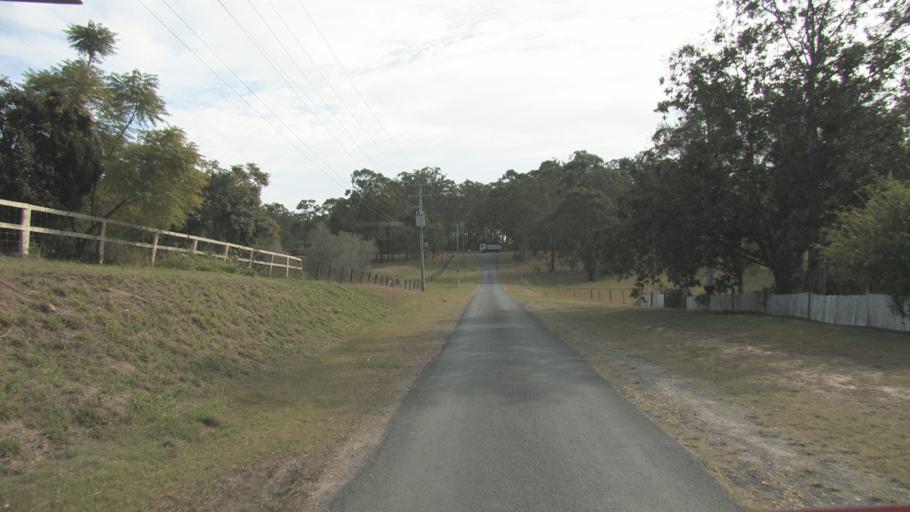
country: AU
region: Queensland
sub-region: Logan
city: Chambers Flat
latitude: -27.7480
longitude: 153.0617
